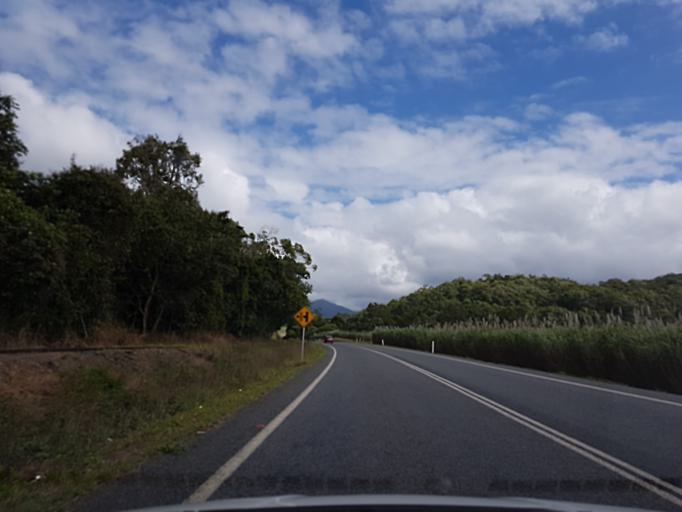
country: AU
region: Queensland
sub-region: Cairns
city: Port Douglas
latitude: -16.4773
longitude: 145.4009
